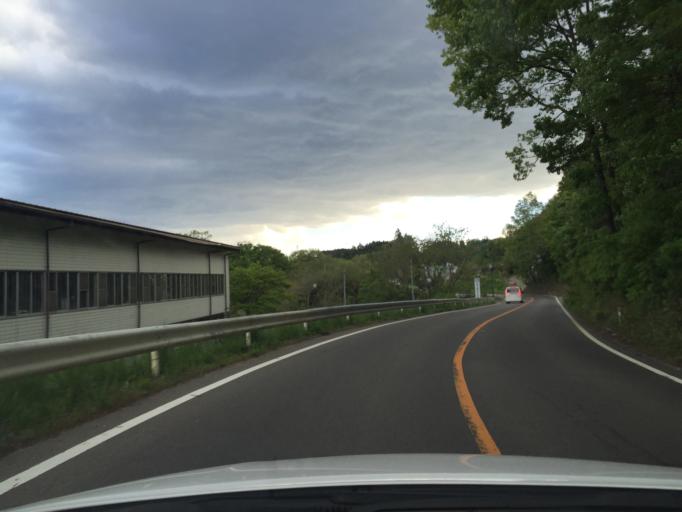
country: JP
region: Fukushima
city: Fukushima-shi
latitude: 37.6621
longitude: 140.5131
